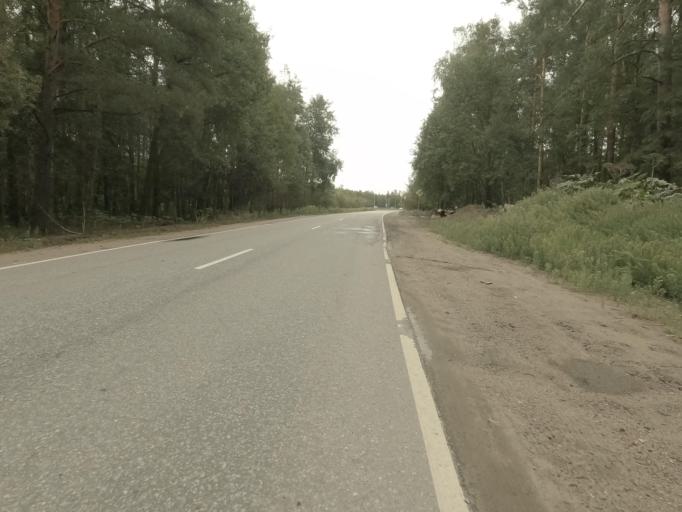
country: RU
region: Leningrad
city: Shcheglovo
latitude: 59.9028
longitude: 30.7747
